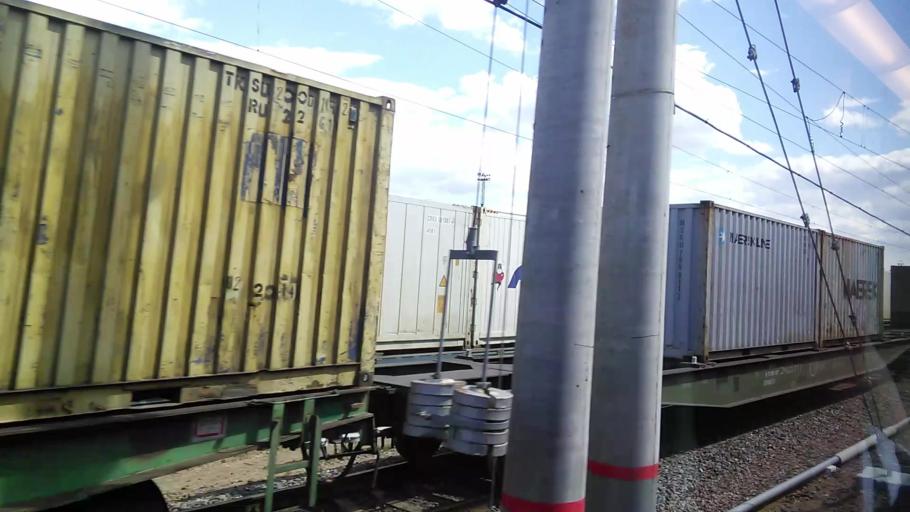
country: RU
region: Moscow
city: Mar'ina Roshcha
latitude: 55.8019
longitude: 37.5883
